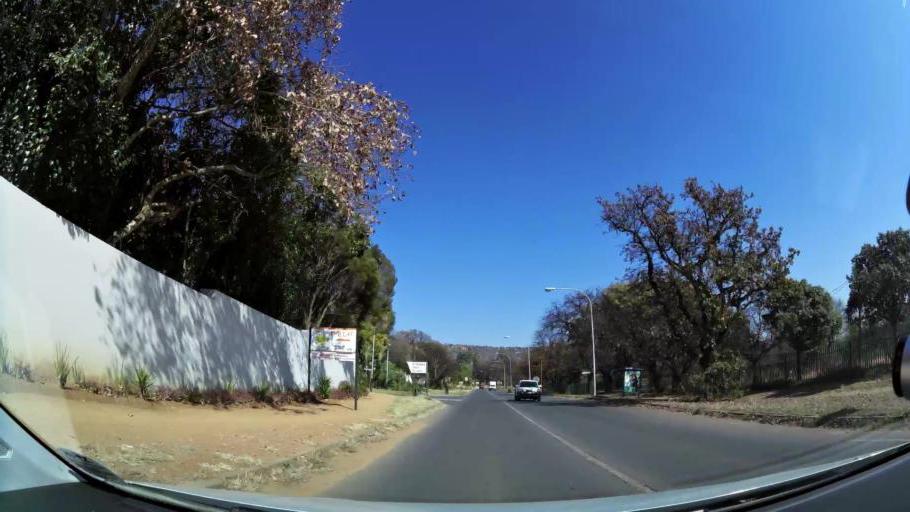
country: ZA
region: Gauteng
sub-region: City of Johannesburg Metropolitan Municipality
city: Modderfontein
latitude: -26.1580
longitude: 28.1189
